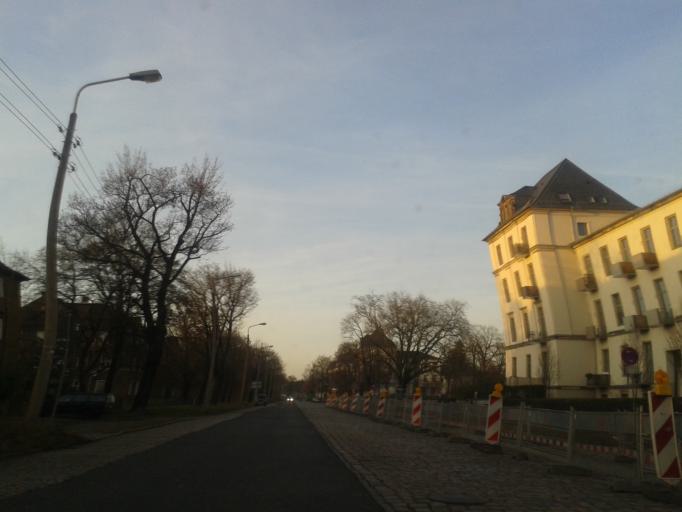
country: DE
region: Saxony
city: Albertstadt
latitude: 51.0814
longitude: 13.7486
